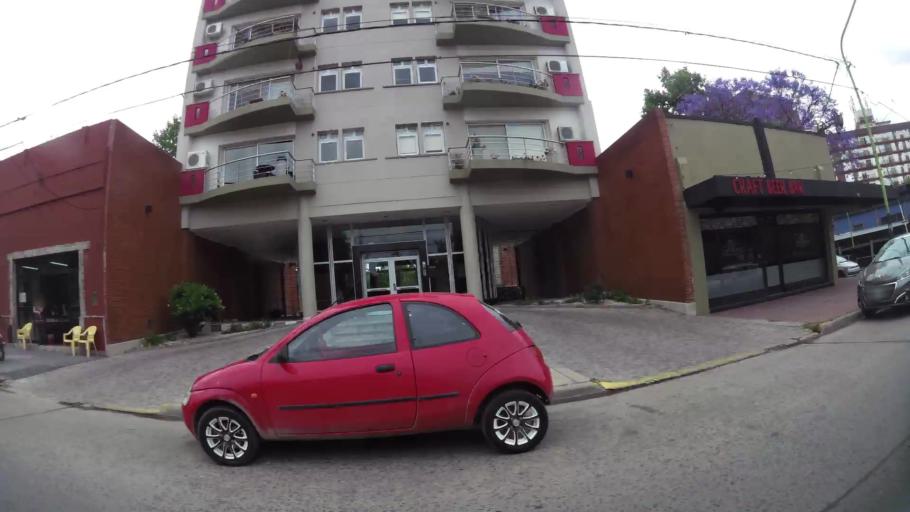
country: AR
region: Buenos Aires
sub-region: Partido de Campana
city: Campana
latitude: -34.1629
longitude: -58.9599
